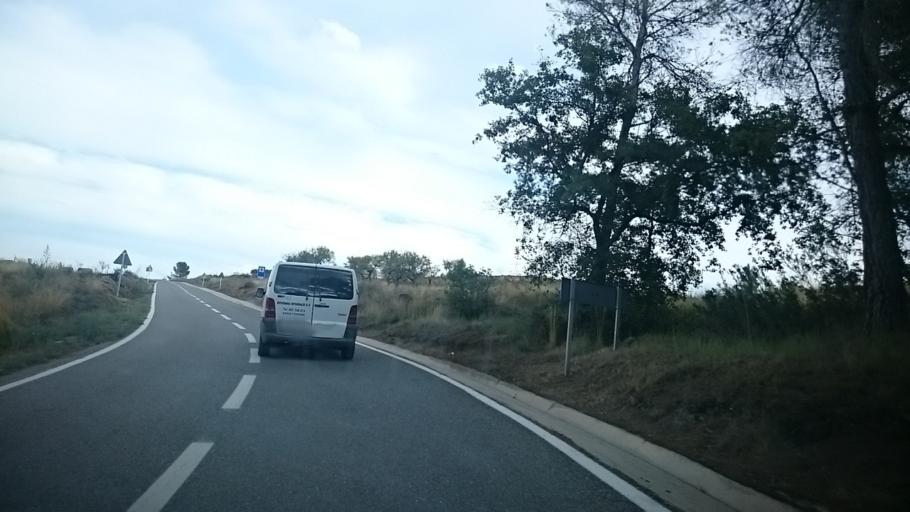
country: ES
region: Catalonia
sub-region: Provincia de Barcelona
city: Odena
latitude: 41.6264
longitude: 1.6677
